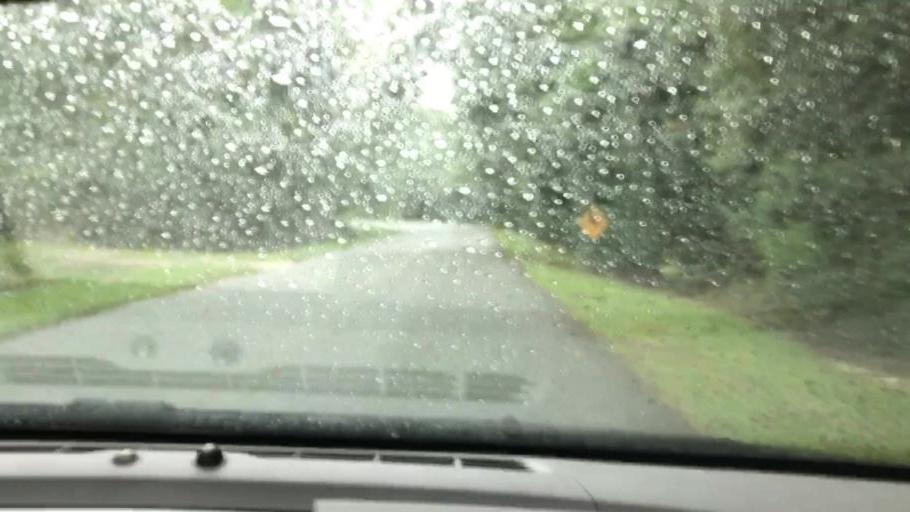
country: US
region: Georgia
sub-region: Clay County
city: Fort Gaines
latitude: 31.6645
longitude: -85.0561
